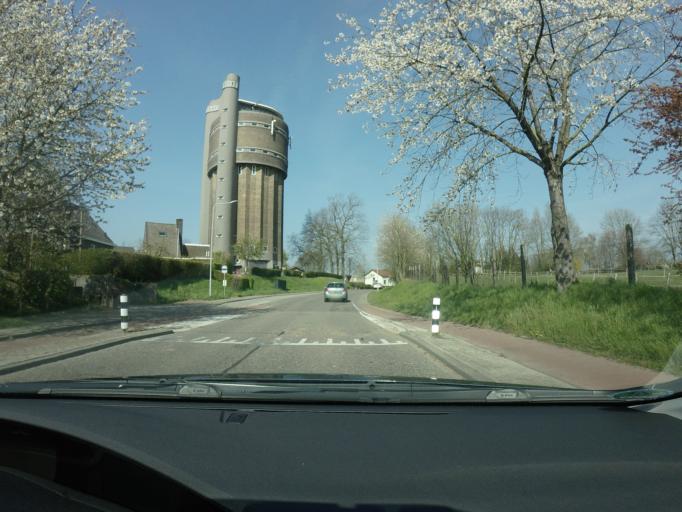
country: NL
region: Limburg
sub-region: Valkenburg aan de Geul
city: Broekhem
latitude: 50.8979
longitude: 5.8252
